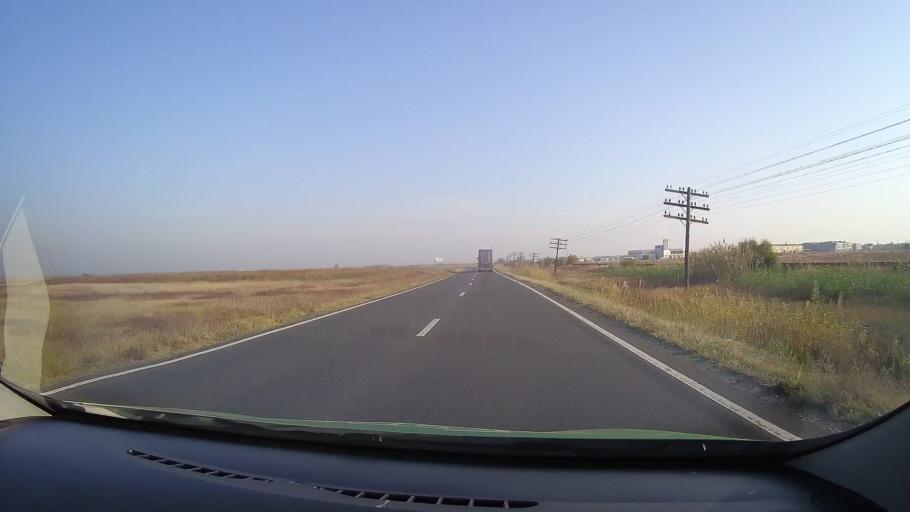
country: RO
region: Arad
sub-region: Comuna Chisineu Cris
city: Nadab
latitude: 46.4760
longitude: 21.4962
